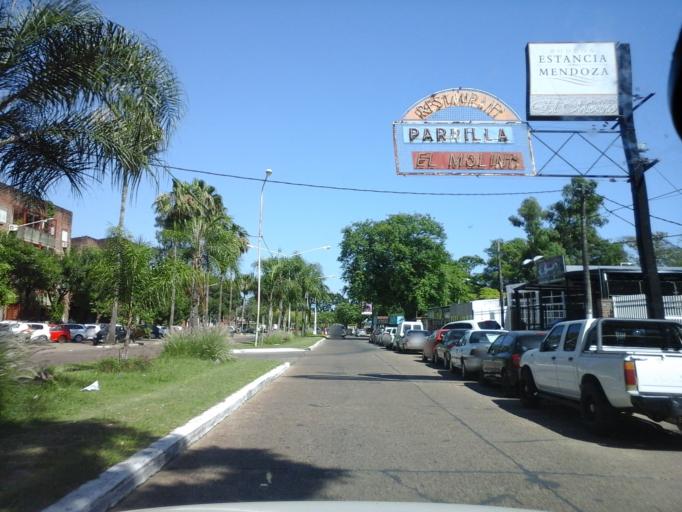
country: AR
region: Corrientes
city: Corrientes
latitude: -27.4618
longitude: -58.8287
